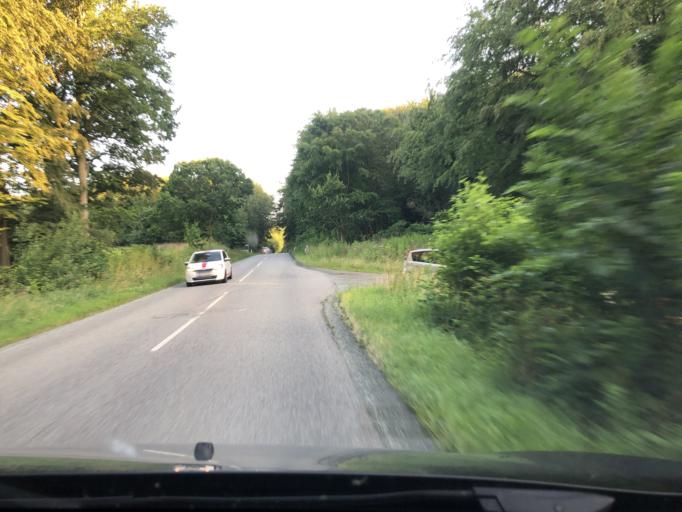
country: DK
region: South Denmark
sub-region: Vejle Kommune
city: Borkop
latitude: 55.6805
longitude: 9.6154
